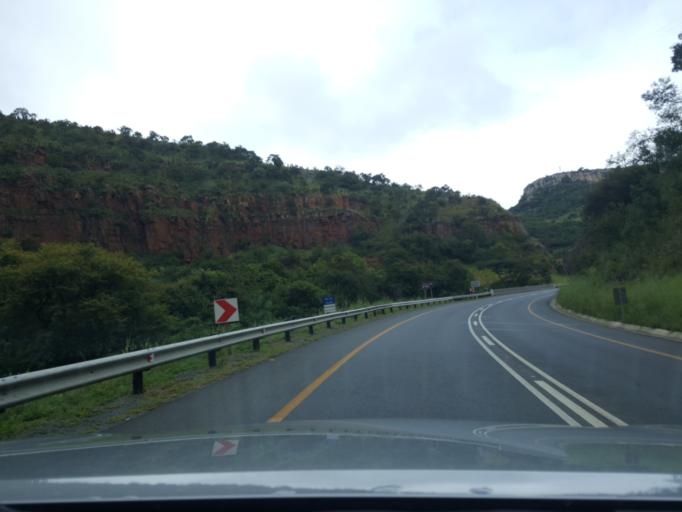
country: ZA
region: Mpumalanga
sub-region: Nkangala District Municipality
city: Belfast
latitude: -25.6475
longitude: 30.3604
